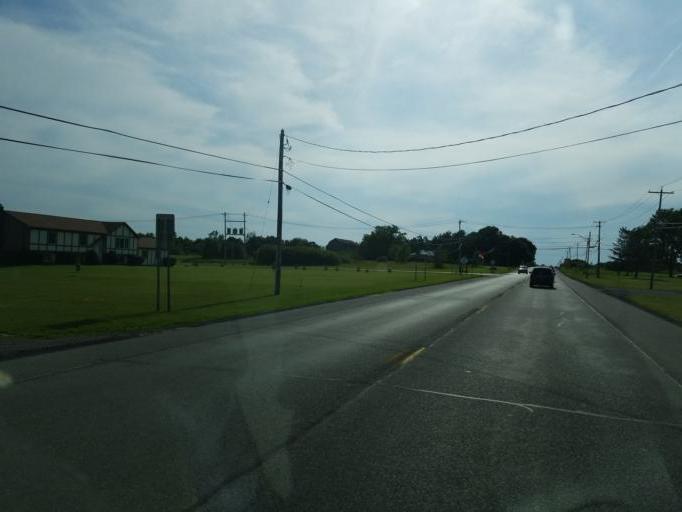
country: US
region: New York
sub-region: Genesee County
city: Le Roy
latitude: 42.9825
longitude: -78.0805
